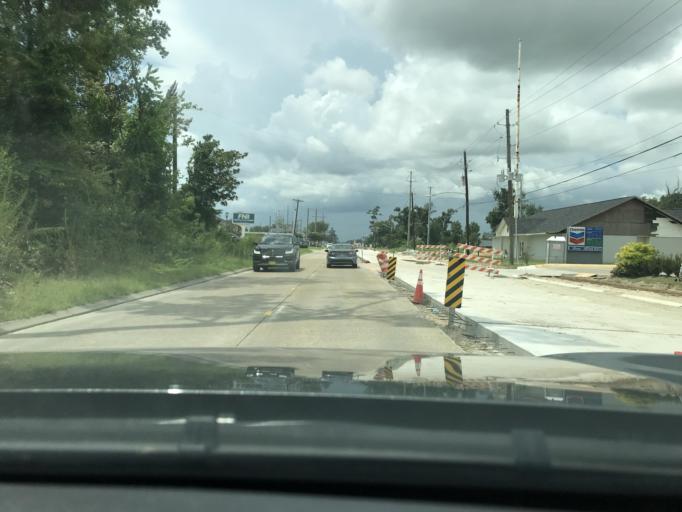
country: US
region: Louisiana
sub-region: Calcasieu Parish
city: Sulphur
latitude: 30.2275
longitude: -93.3391
